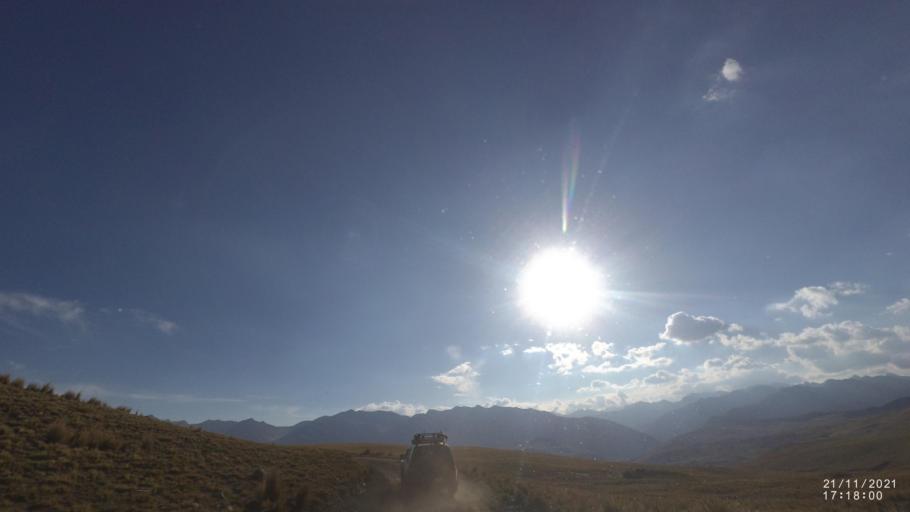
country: BO
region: Cochabamba
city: Cochabamba
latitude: -17.1442
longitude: -66.2572
